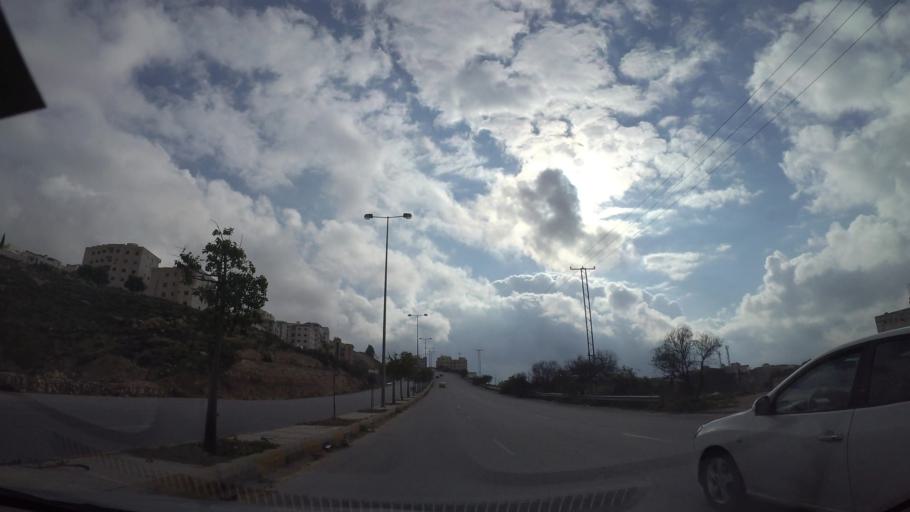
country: JO
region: Amman
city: Al Jubayhah
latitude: 32.0679
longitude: 35.8725
